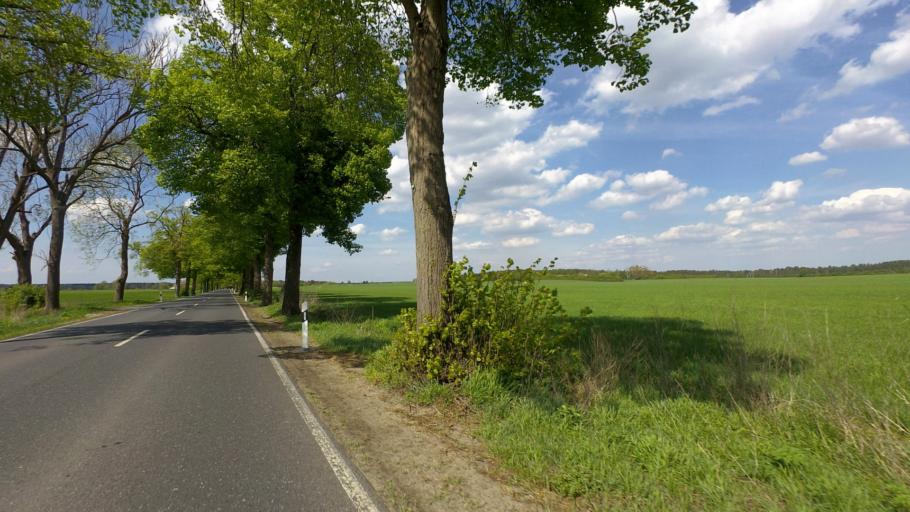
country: DE
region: Brandenburg
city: Marienwerder
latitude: 52.8916
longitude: 13.5418
